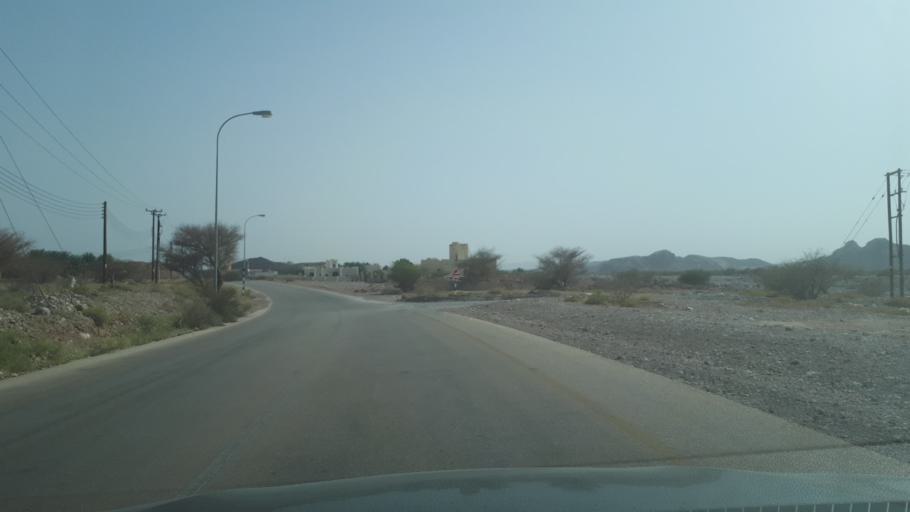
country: OM
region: Az Zahirah
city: `Ibri
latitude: 23.1639
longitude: 56.9139
